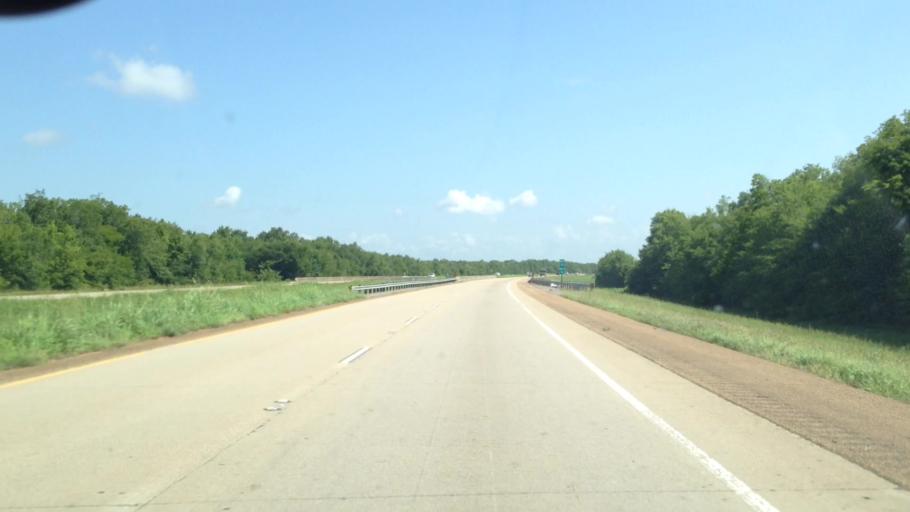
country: US
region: Louisiana
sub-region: Rapides Parish
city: Woodworth
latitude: 31.1964
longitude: -92.4741
